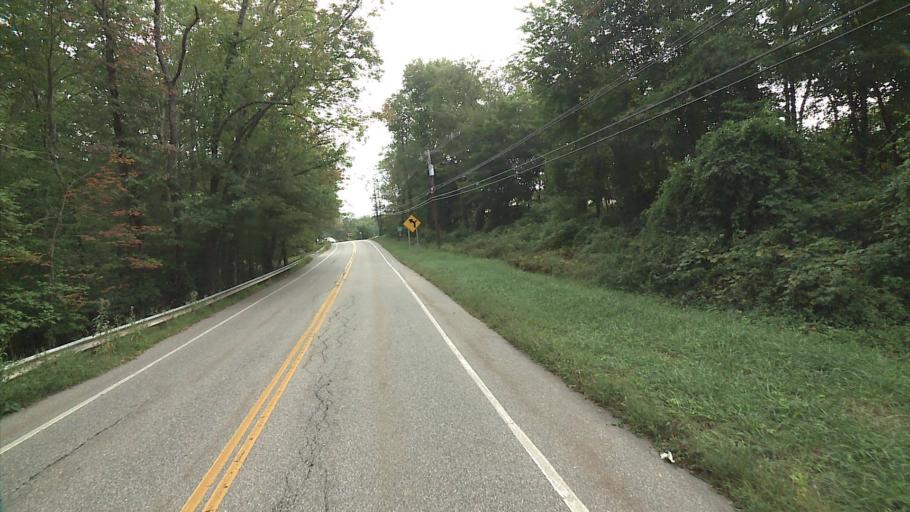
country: US
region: Connecticut
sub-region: Tolland County
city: Storrs
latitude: 41.7951
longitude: -72.2526
